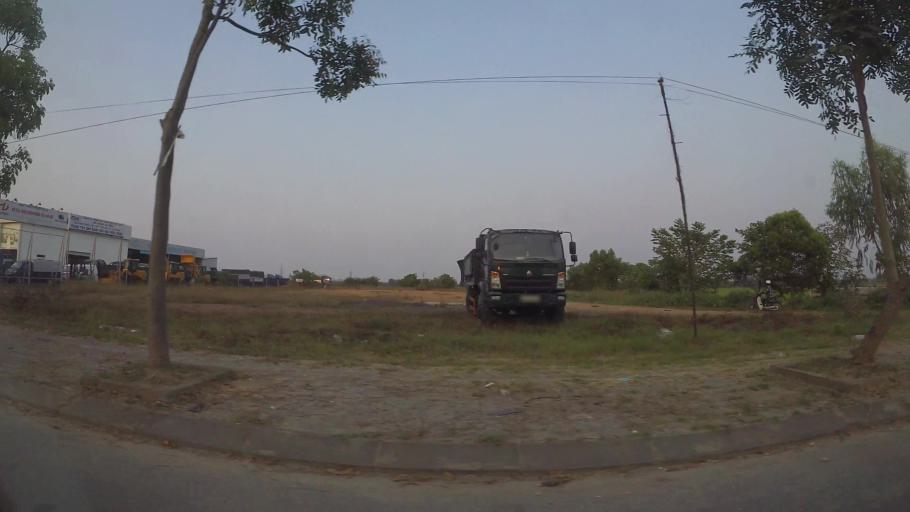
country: VN
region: Da Nang
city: Cam Le
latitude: 15.9650
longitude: 108.2119
